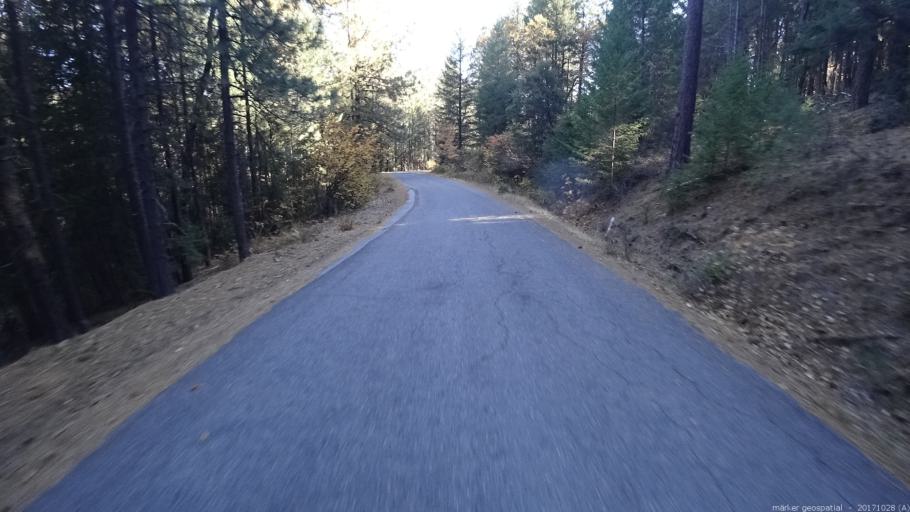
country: US
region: California
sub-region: Trinity County
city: Lewiston
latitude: 40.8106
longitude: -122.6284
